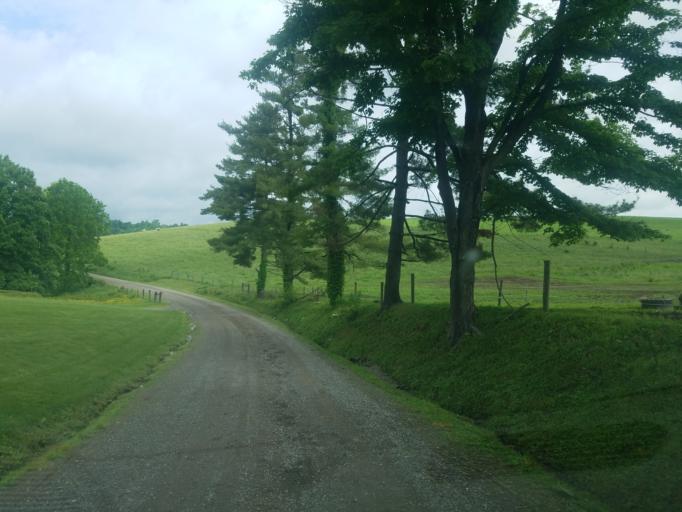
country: US
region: Ohio
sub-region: Holmes County
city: Millersburg
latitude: 40.4730
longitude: -81.8010
